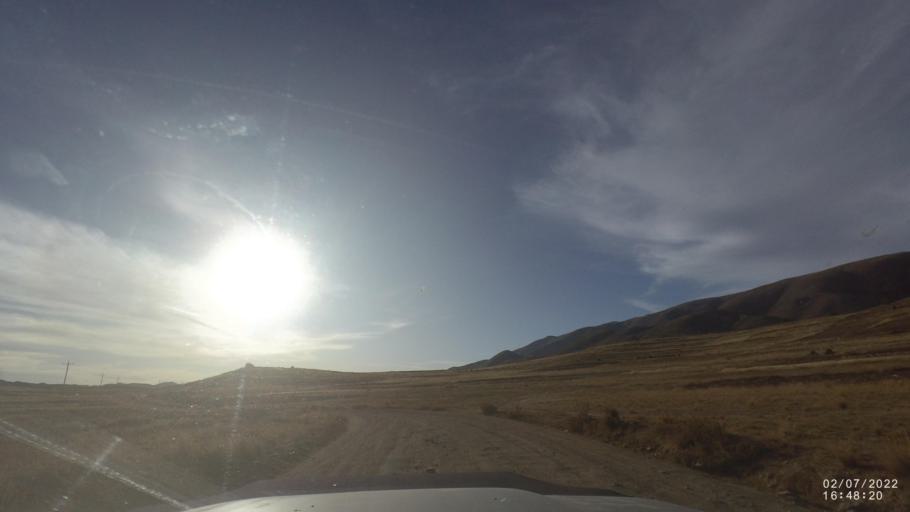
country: BO
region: Cochabamba
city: Irpa Irpa
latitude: -17.9781
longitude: -66.5184
